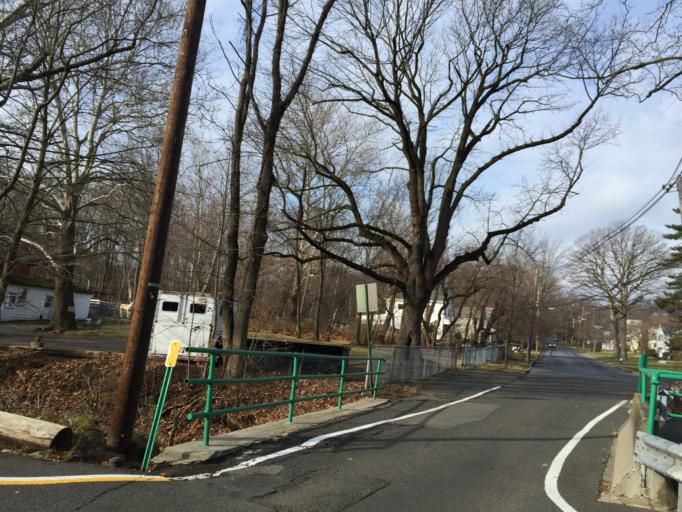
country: US
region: New Jersey
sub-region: Union County
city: Springfield
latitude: 40.7106
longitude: -74.3396
